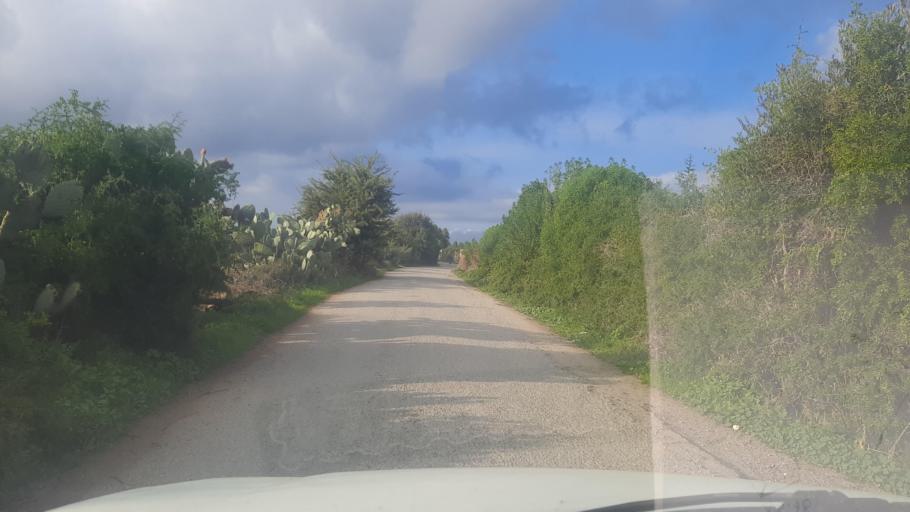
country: TN
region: Nabul
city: Manzil Bu Zalafah
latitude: 36.7112
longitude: 10.5005
